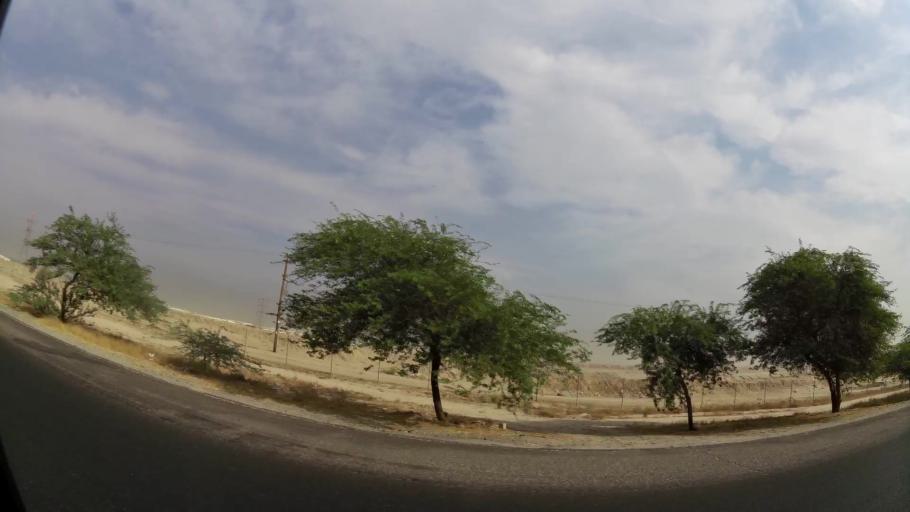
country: KW
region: Muhafazat al Jahra'
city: Al Jahra'
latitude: 29.2923
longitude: 47.7537
